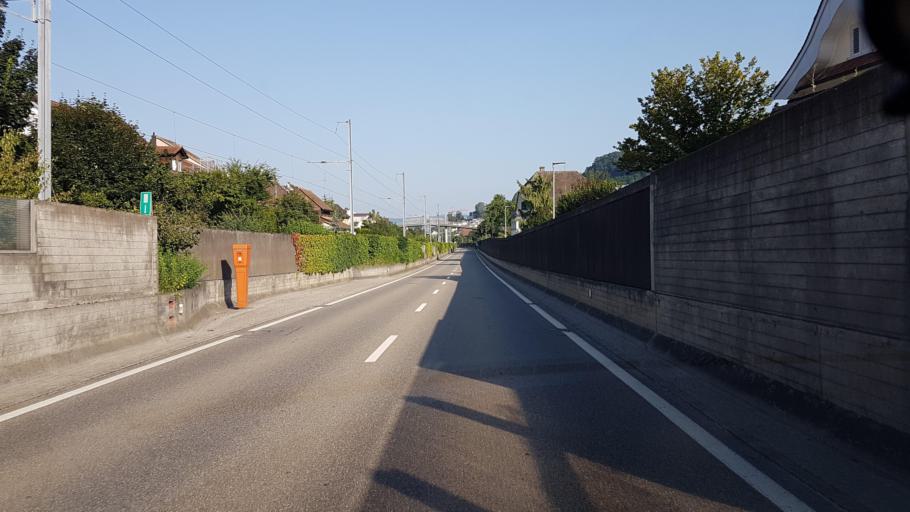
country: CH
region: Aargau
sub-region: Bezirk Zurzach
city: Klingnau
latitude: 47.5789
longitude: 8.2547
